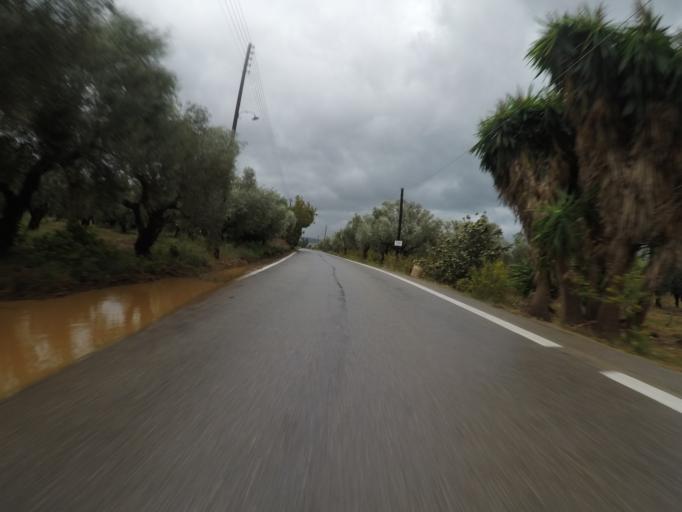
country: GR
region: Peloponnese
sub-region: Nomos Messinias
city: Pylos
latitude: 36.9793
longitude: 21.6851
